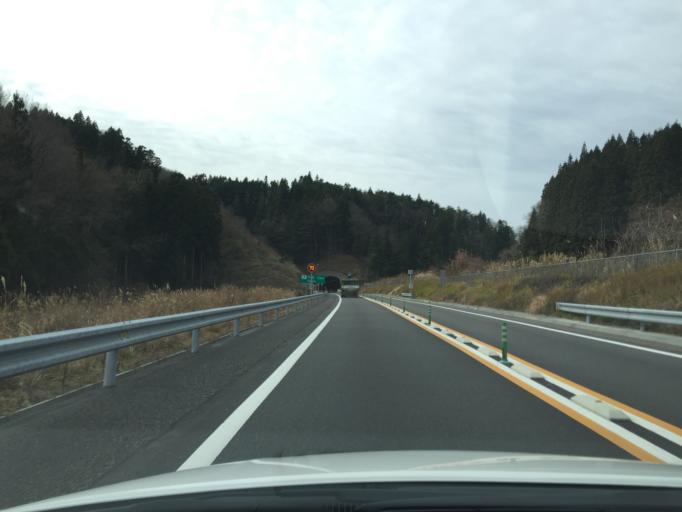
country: JP
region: Fukushima
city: Ishikawa
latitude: 37.2660
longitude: 140.5731
